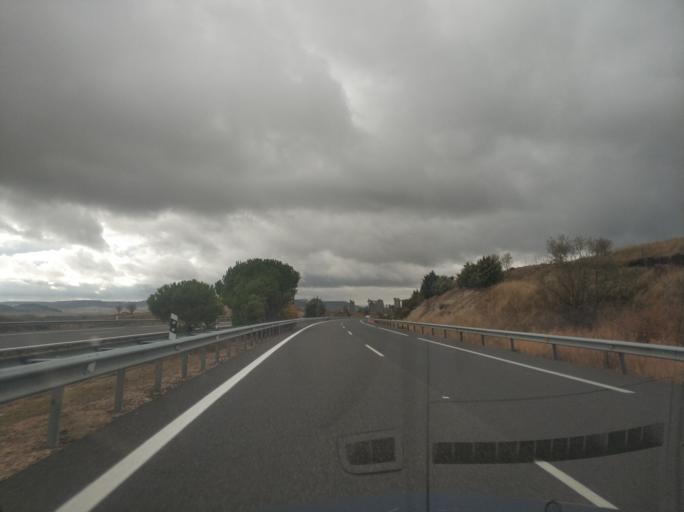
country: ES
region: Castille and Leon
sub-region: Provincia de Palencia
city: Soto de Cerrato
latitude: 41.9588
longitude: -4.4580
